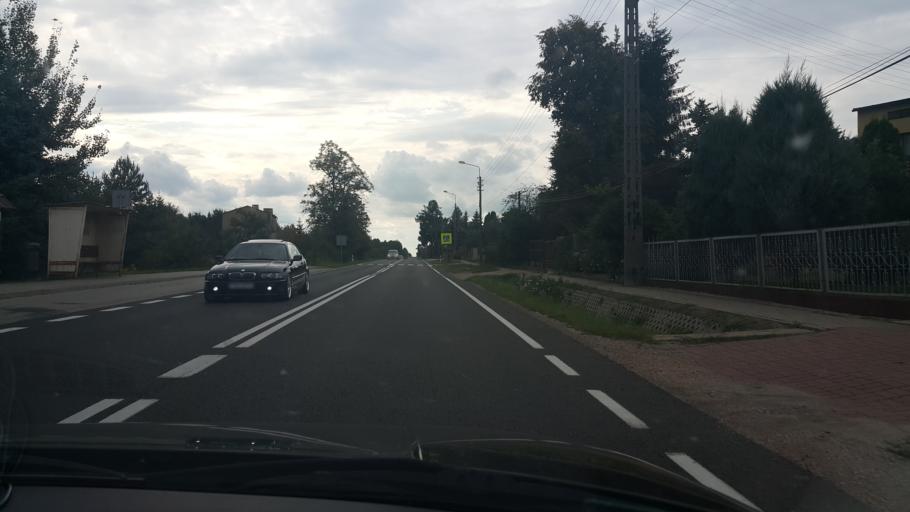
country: PL
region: Swietokrzyskie
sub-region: Powiat skarzyski
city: Blizyn
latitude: 51.1001
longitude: 20.7924
